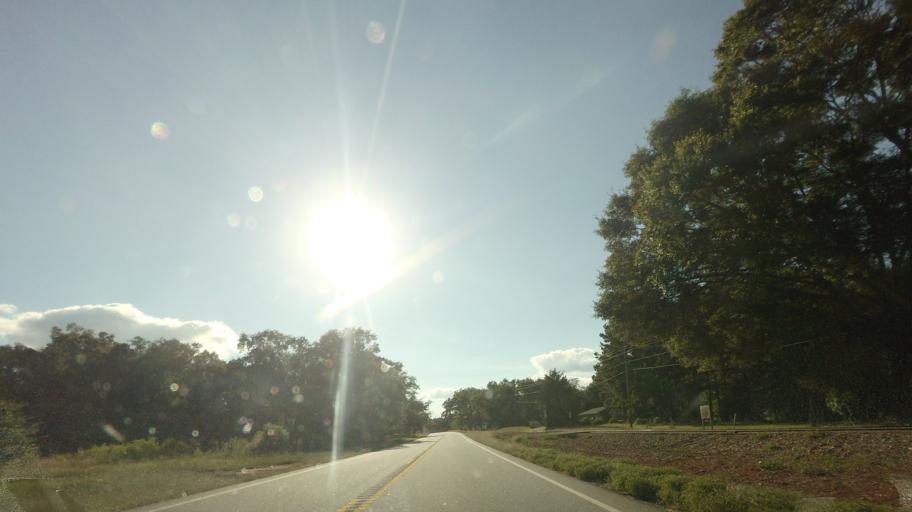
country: US
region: Georgia
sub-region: Upson County
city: Hannahs Mill
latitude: 32.9646
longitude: -84.2369
